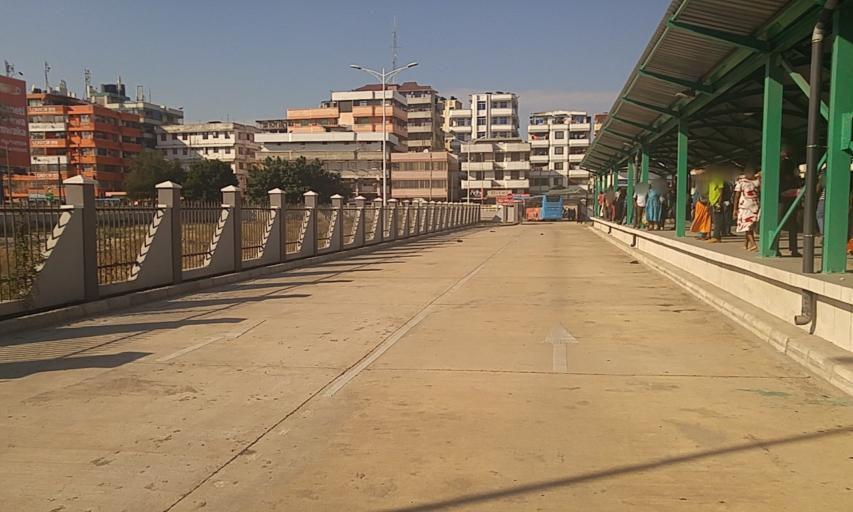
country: TZ
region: Dar es Salaam
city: Dar es Salaam
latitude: -6.8255
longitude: 39.2736
